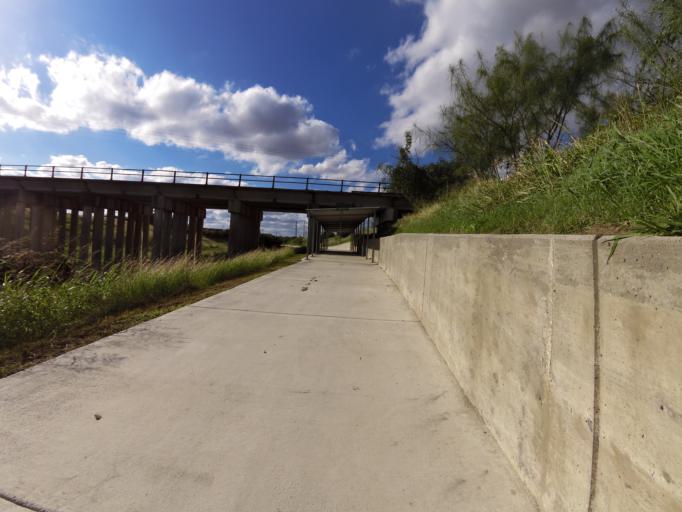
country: US
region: Texas
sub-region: Bexar County
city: San Antonio
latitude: 29.4130
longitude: -98.5098
